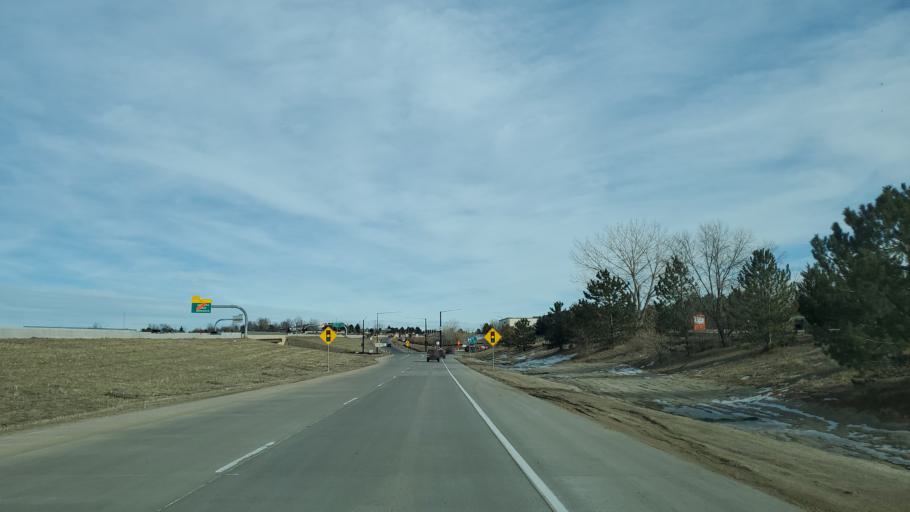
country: US
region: Colorado
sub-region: Douglas County
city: Highlands Ranch
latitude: 39.5631
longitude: -104.9900
